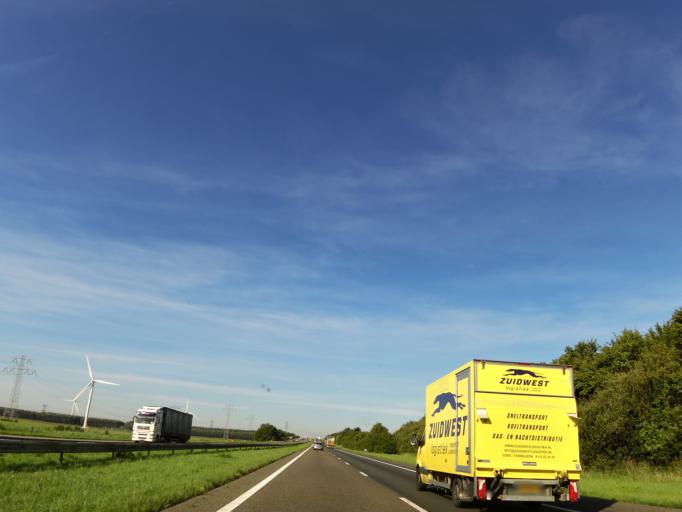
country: NL
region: North Brabant
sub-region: Gemeente Woensdrecht
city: Woensdrecht
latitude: 51.4292
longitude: 4.2511
